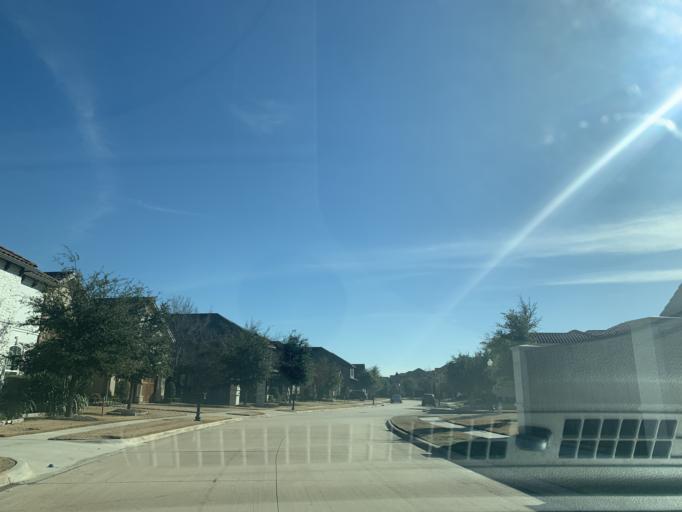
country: US
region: Texas
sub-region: Denton County
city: The Colony
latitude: 33.0596
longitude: -96.8161
